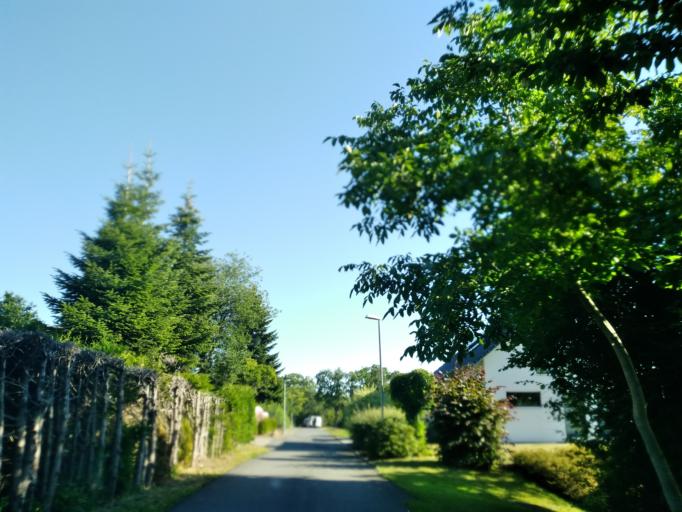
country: DE
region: Baden-Wuerttemberg
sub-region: Karlsruhe Region
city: Limbach
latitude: 49.4805
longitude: 9.2094
